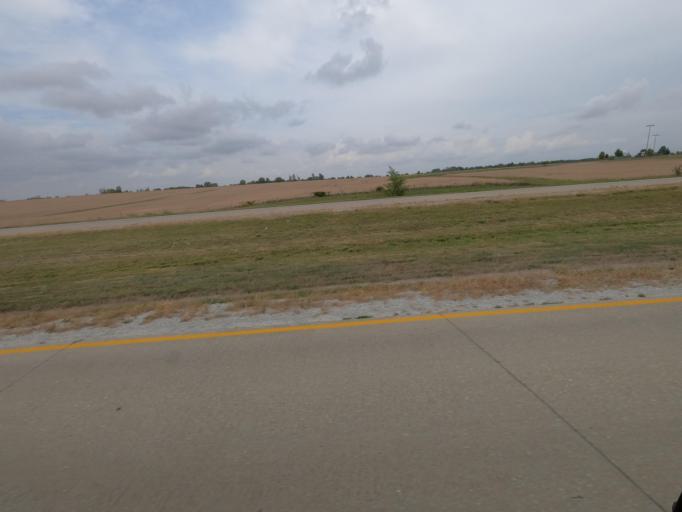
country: US
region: Iowa
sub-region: Jasper County
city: Monroe
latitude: 41.5112
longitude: -93.1160
